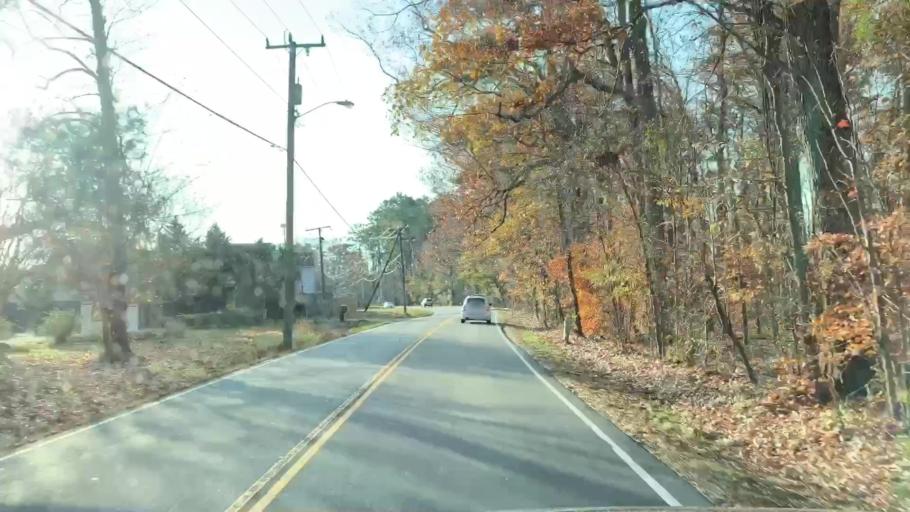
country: US
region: Virginia
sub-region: City of Chesapeake
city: Chesapeake
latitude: 36.7651
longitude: -76.1493
